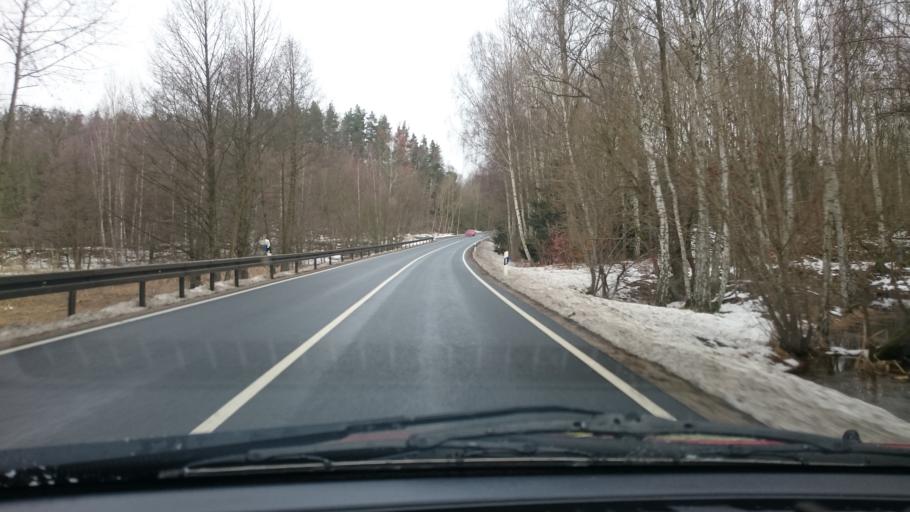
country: DE
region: Saxony
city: Waldkirchen
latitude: 50.5796
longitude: 12.3920
